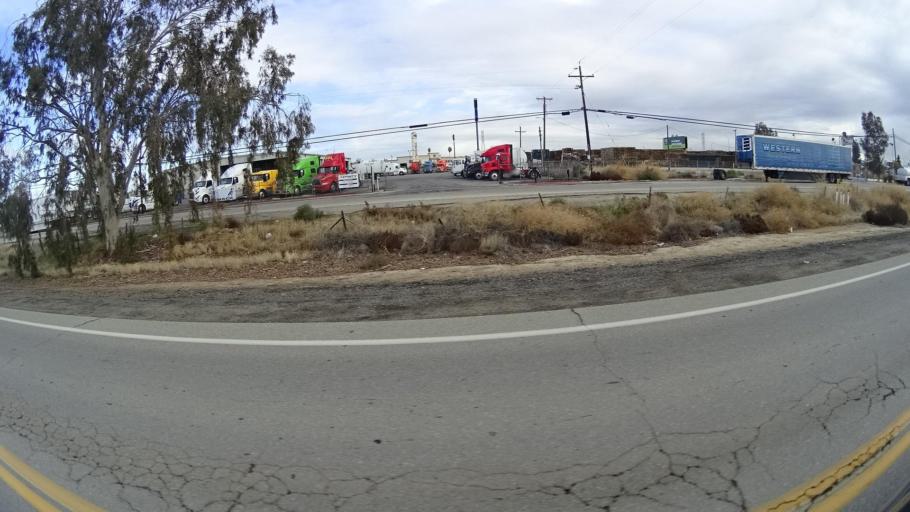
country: US
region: California
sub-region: Kern County
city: Greenacres
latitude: 35.4385
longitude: -119.0835
